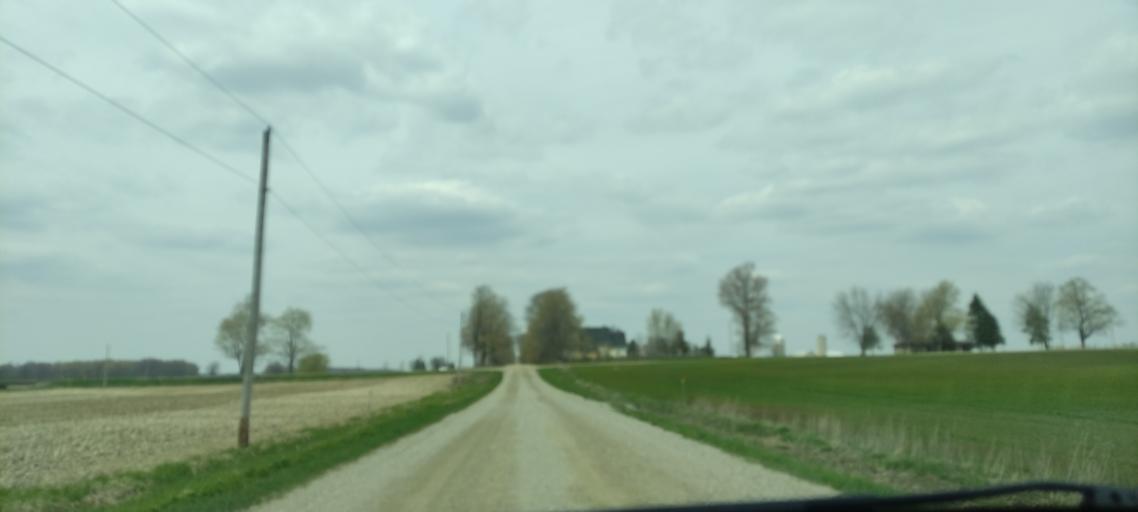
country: CA
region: Ontario
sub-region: Oxford County
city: Woodstock
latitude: 43.2848
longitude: -80.7476
